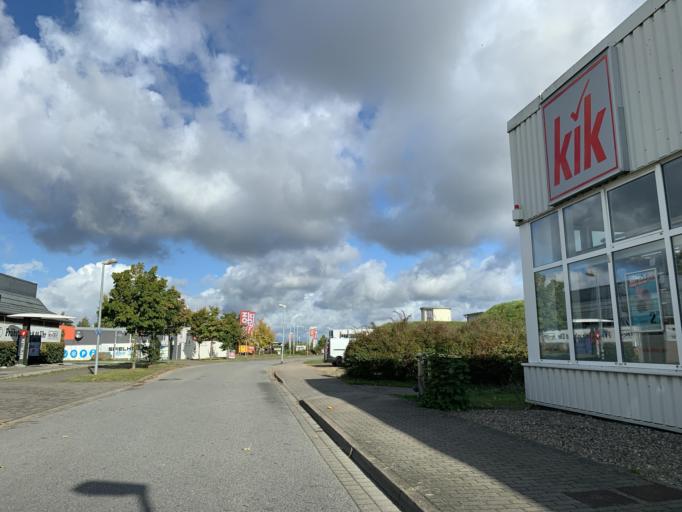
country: DE
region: Mecklenburg-Vorpommern
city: Neubrandenburg
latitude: 53.5186
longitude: 13.2611
